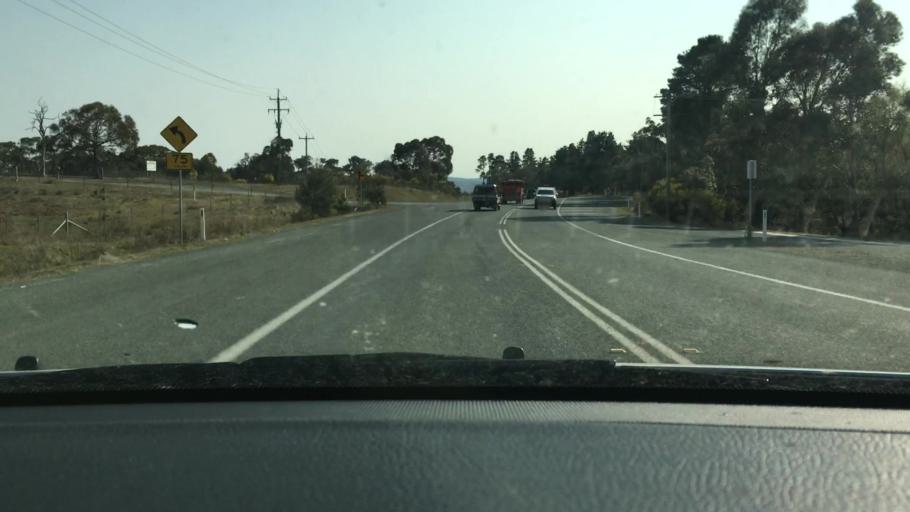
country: AU
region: New South Wales
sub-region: Queanbeyan
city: Queanbeyan
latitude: -35.4040
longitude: 149.2296
